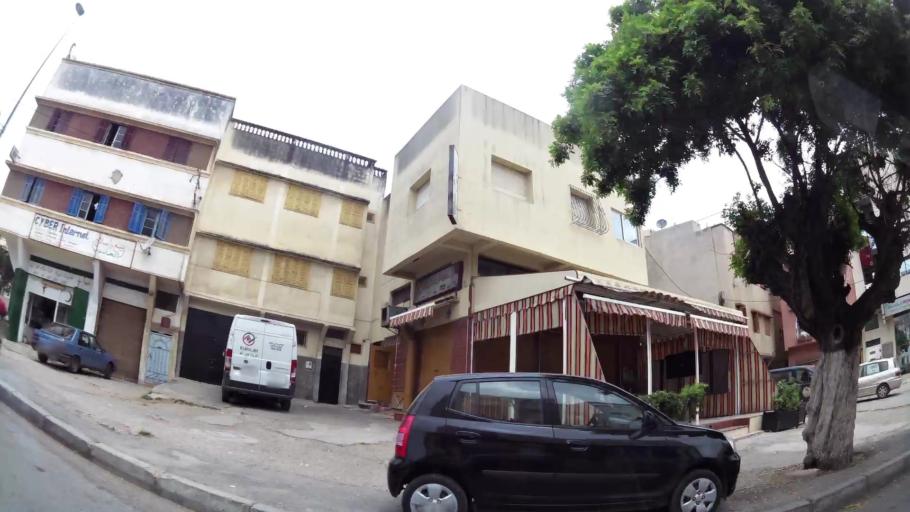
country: MA
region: Rabat-Sale-Zemmour-Zaer
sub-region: Rabat
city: Rabat
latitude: 34.0006
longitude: -6.8645
